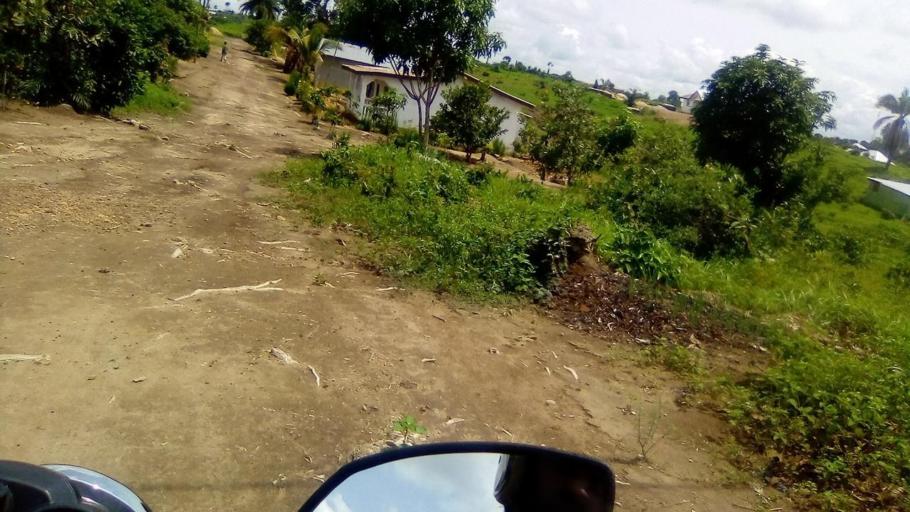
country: SL
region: Southern Province
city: Bo
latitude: 7.9348
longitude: -11.7452
